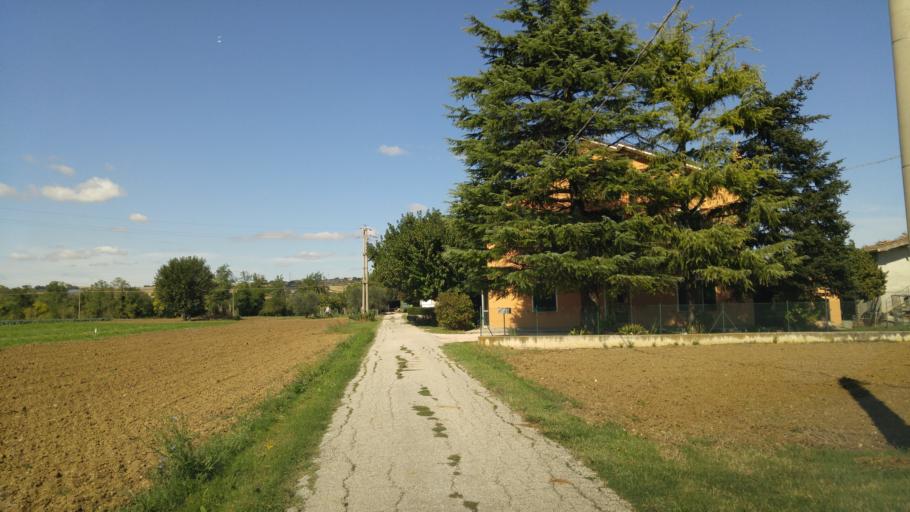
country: IT
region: The Marches
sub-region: Provincia di Pesaro e Urbino
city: Cuccurano
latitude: 43.7780
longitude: 12.9566
